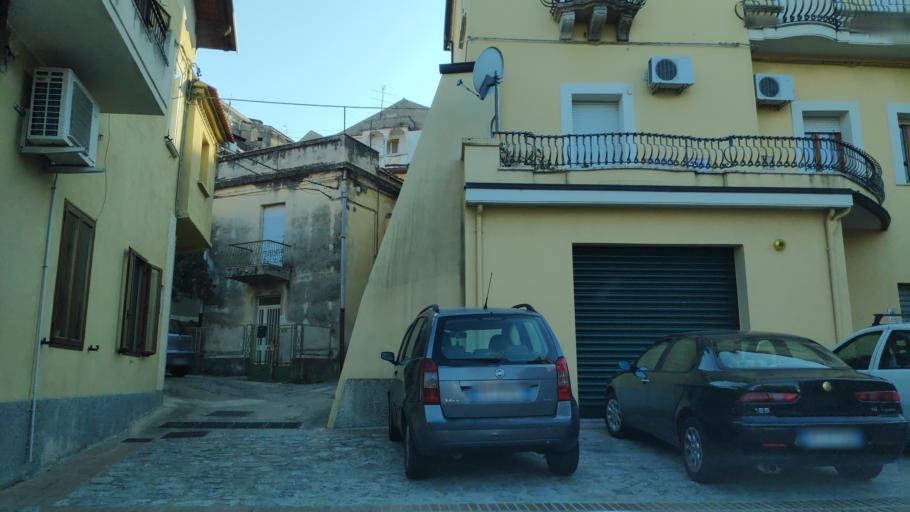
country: IT
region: Calabria
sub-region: Provincia di Catanzaro
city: Satriano
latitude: 38.6676
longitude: 16.4820
